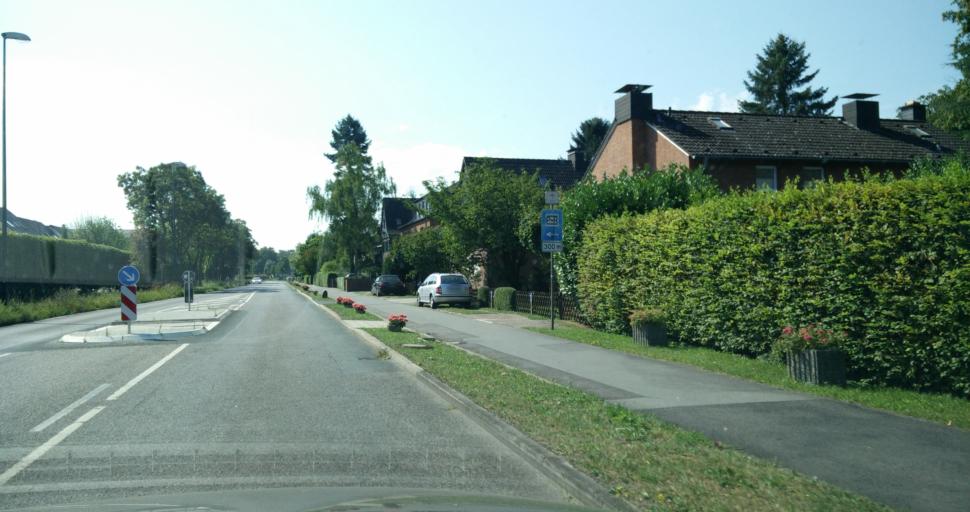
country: DE
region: North Rhine-Westphalia
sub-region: Regierungsbezirk Dusseldorf
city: Meerbusch
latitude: 51.3216
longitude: 6.7439
